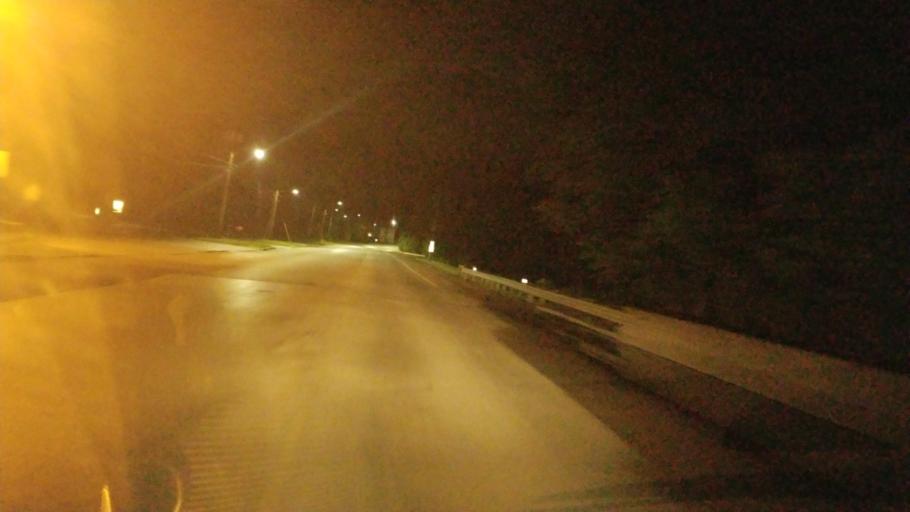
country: US
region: Ohio
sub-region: Trumbull County
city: Niles
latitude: 41.1705
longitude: -80.7671
